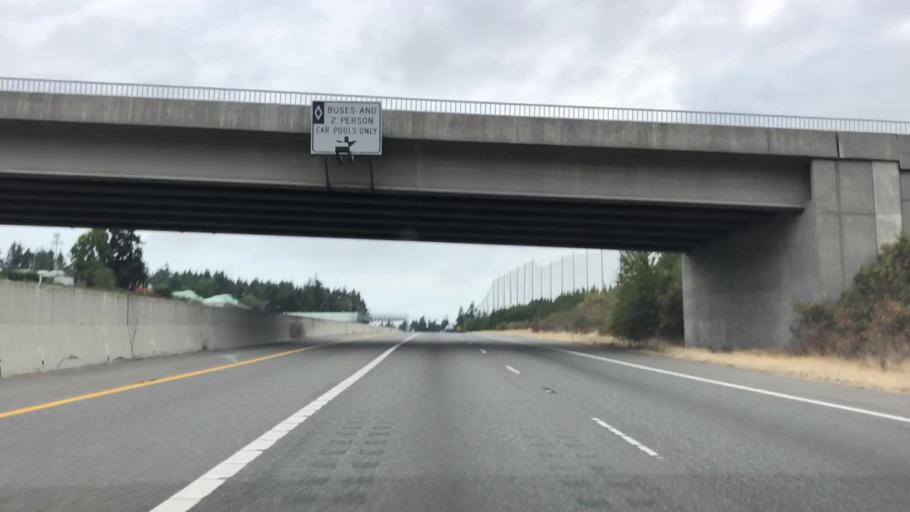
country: US
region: Washington
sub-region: Pierce County
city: Wollochet
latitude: 47.2797
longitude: -122.5602
